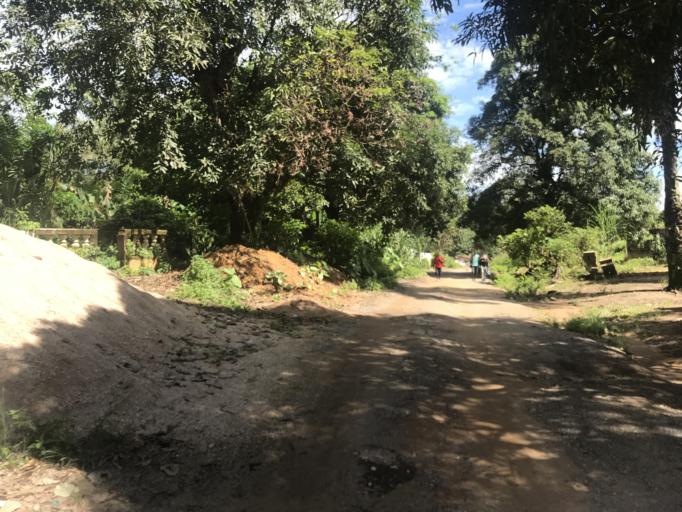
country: SL
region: Eastern Province
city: Koidu
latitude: 8.6422
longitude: -10.9879
